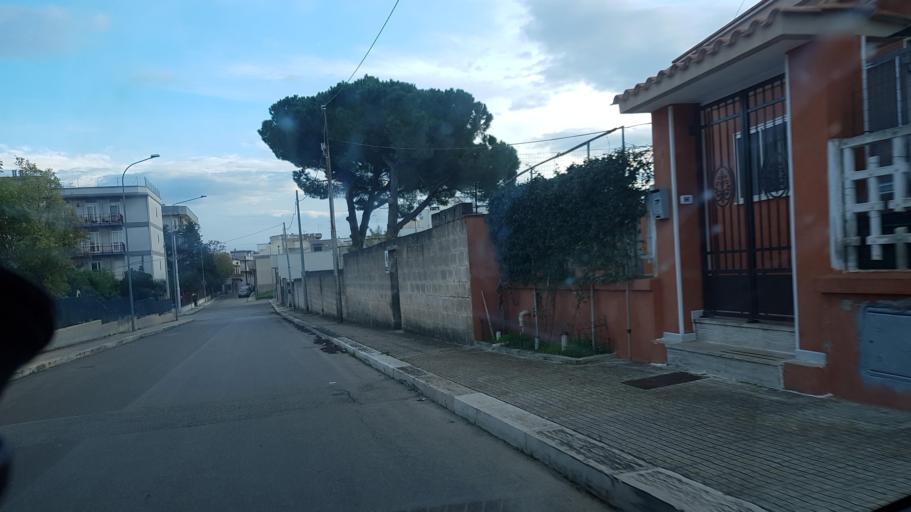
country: IT
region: Apulia
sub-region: Provincia di Brindisi
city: San Vito dei Normanni
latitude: 40.6584
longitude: 17.6972
